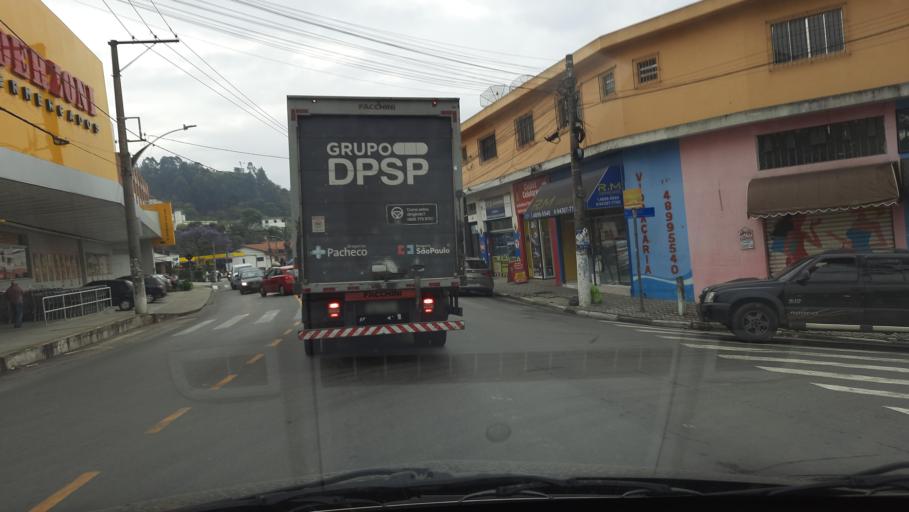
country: BR
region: Sao Paulo
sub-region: Caieiras
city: Caieiras
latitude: -23.3940
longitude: -46.7152
